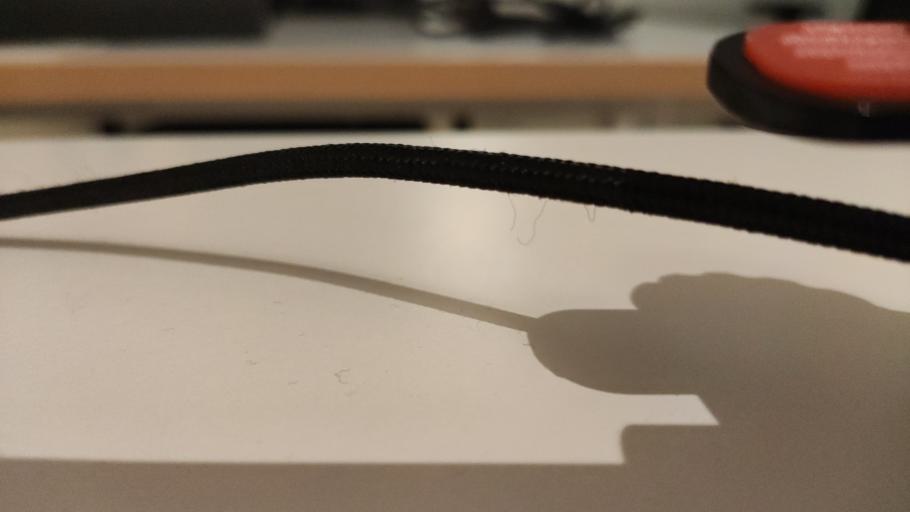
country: RU
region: Moskovskaya
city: Kurovskoye
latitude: 55.5975
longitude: 38.9246
